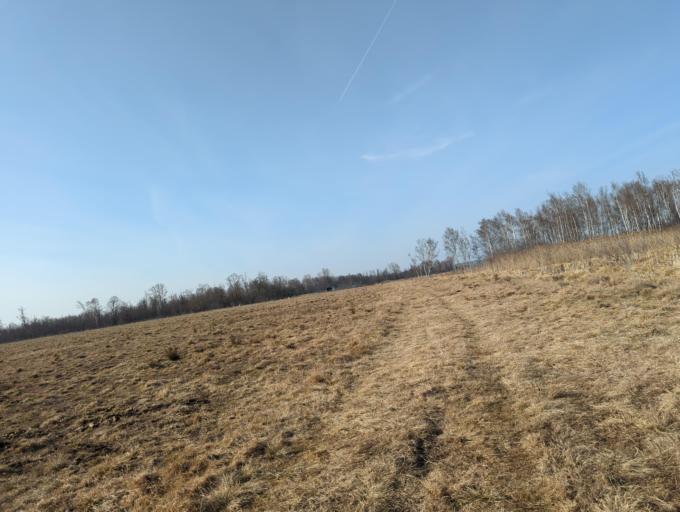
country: DE
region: Bavaria
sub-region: Swabia
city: Leipheim
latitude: 48.4855
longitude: 10.2146
